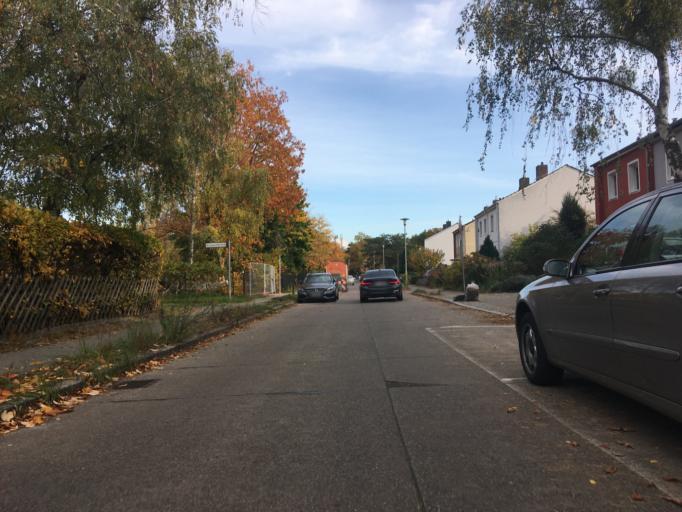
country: DE
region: Berlin
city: Zehlendorf Bezirk
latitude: 52.4213
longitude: 13.2414
